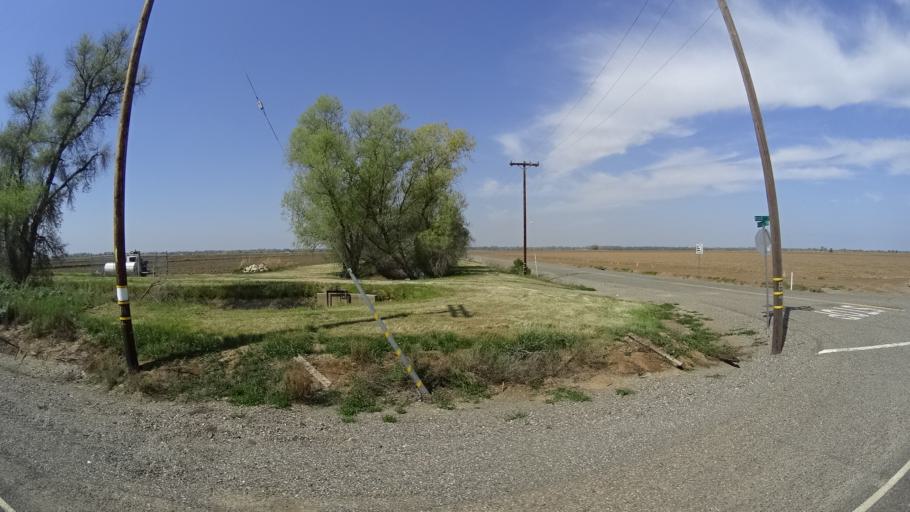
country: US
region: California
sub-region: Butte County
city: Durham
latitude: 39.5223
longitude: -121.9299
